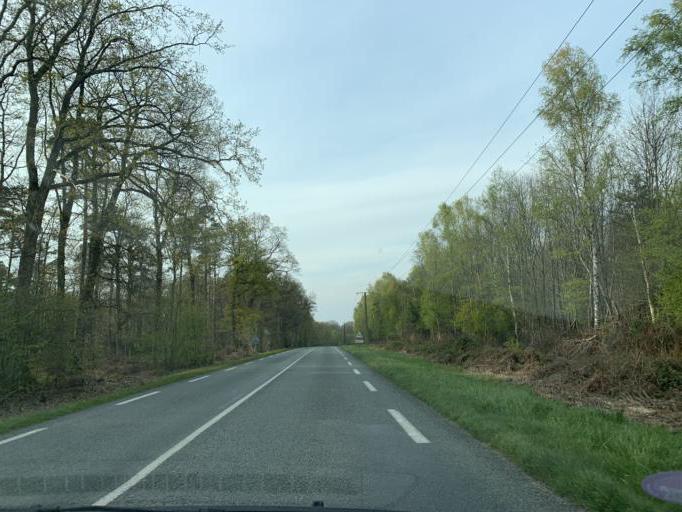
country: FR
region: Haute-Normandie
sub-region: Departement de la Seine-Maritime
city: Jumieges
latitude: 49.4261
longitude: 0.7916
